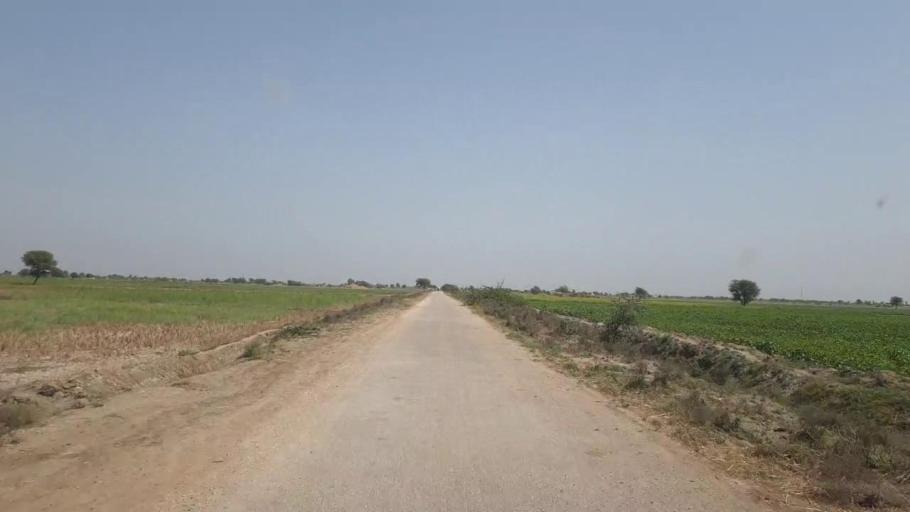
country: PK
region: Sindh
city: Jati
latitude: 24.4774
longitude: 68.5564
